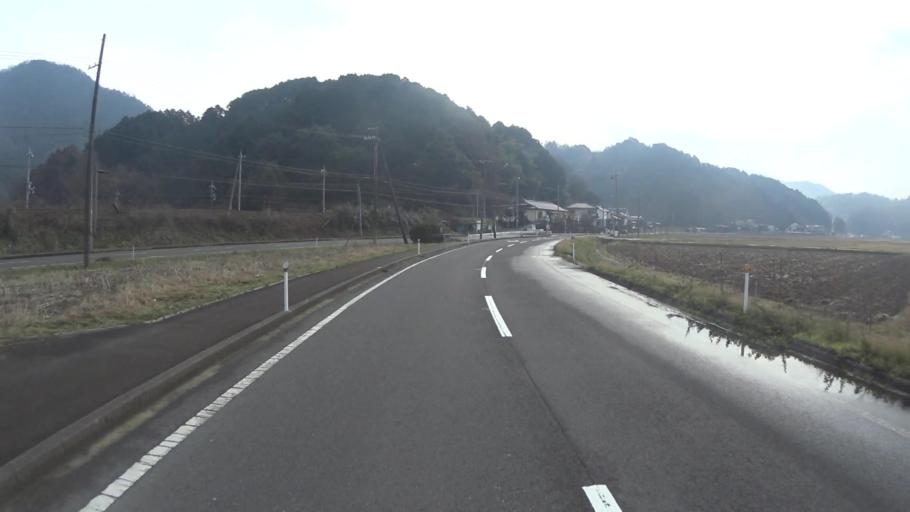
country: JP
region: Kyoto
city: Maizuru
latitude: 35.4620
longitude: 135.2870
